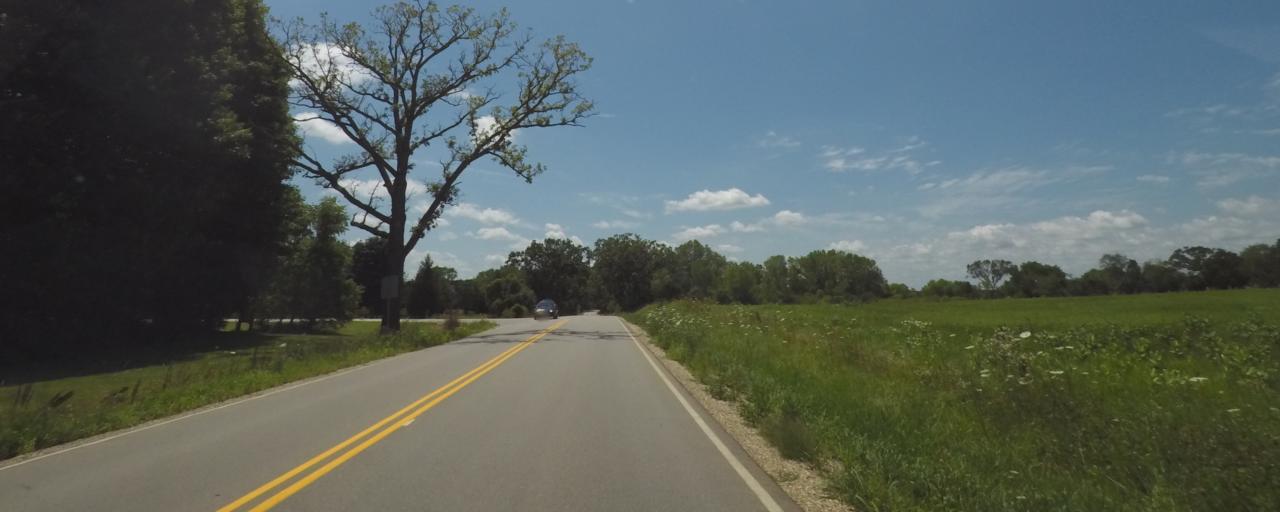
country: US
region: Wisconsin
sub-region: Waukesha County
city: Dousman
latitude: 42.9582
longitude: -88.4703
